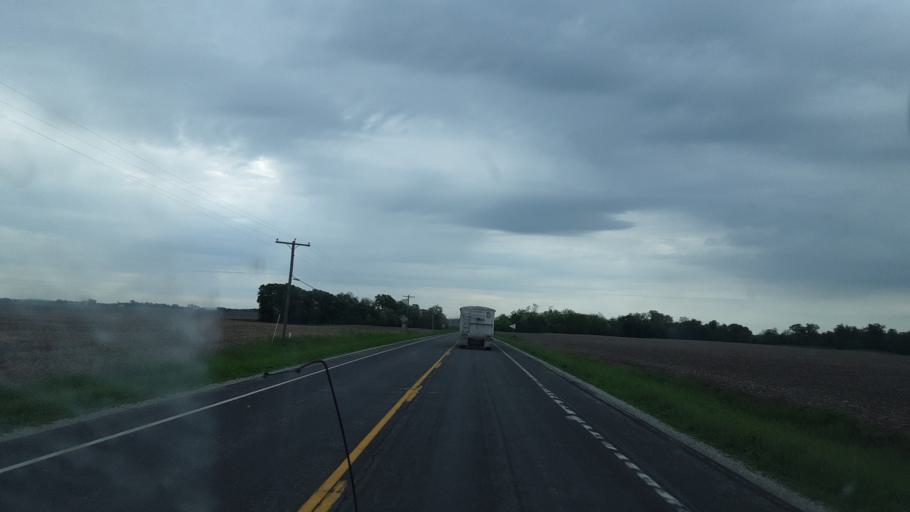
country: US
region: Illinois
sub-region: Fulton County
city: Lewistown
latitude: 40.3482
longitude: -90.2753
